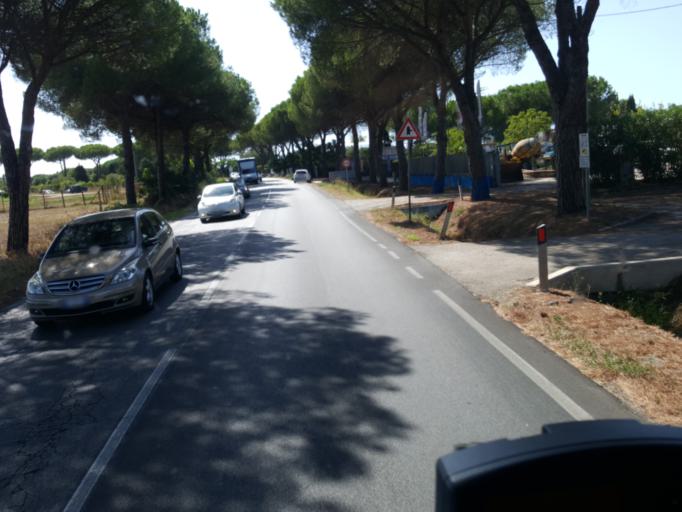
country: IT
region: Latium
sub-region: Provincia di Latina
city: Genio Civile
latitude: 41.5369
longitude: 12.7162
